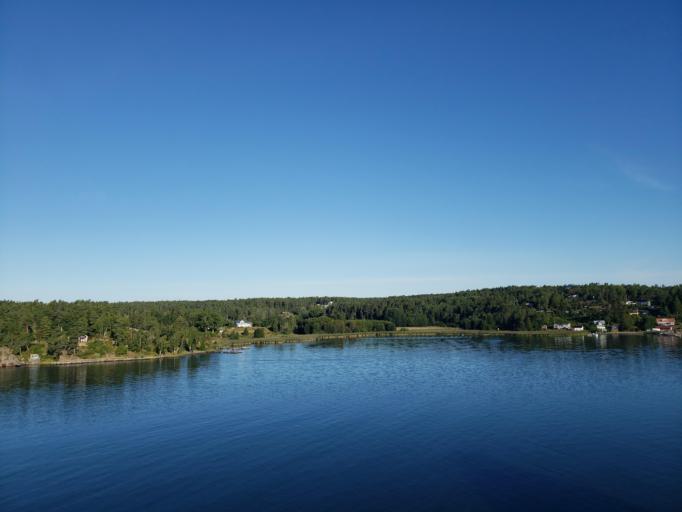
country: SE
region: Stockholm
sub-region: Vaxholms Kommun
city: Vaxholm
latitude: 59.4982
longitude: 18.4662
